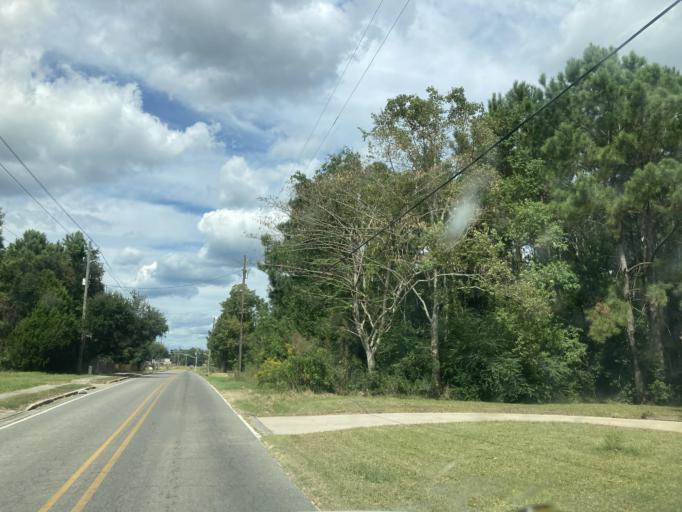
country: US
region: Mississippi
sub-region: Jackson County
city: Saint Martin
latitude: 30.4355
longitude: -88.8809
